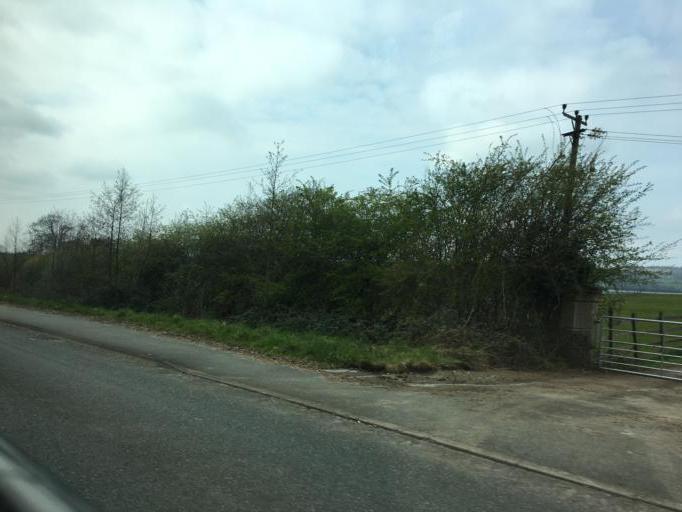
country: GB
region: Wales
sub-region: Gwynedd
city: Y Felinheli
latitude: 53.1706
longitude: -4.2319
